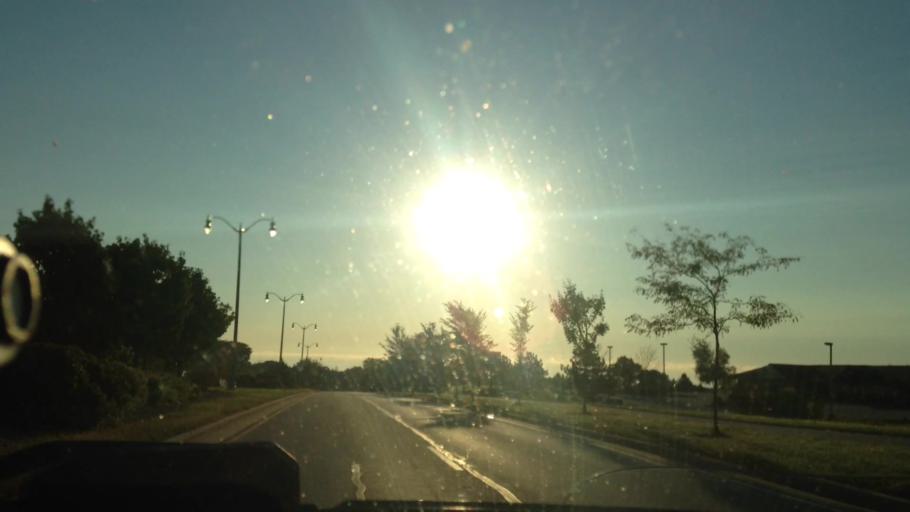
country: US
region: Wisconsin
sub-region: Ozaukee County
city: Port Washington
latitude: 43.3869
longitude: -87.9066
